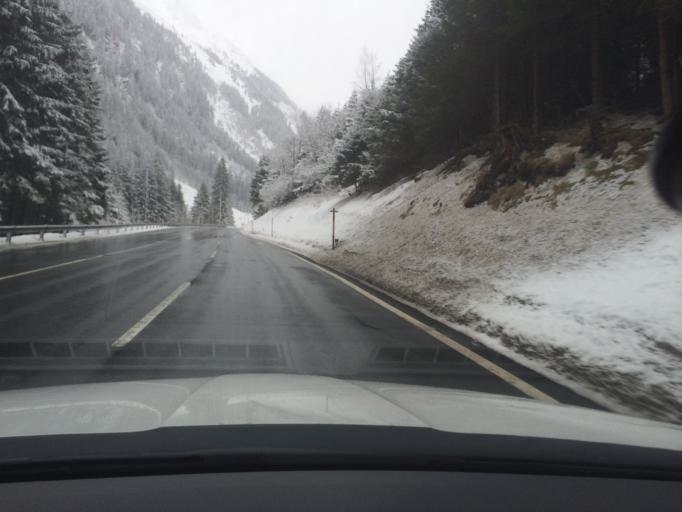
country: AT
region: Salzburg
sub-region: Politischer Bezirk Zell am See
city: Mittersill
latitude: 47.2189
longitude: 12.4998
